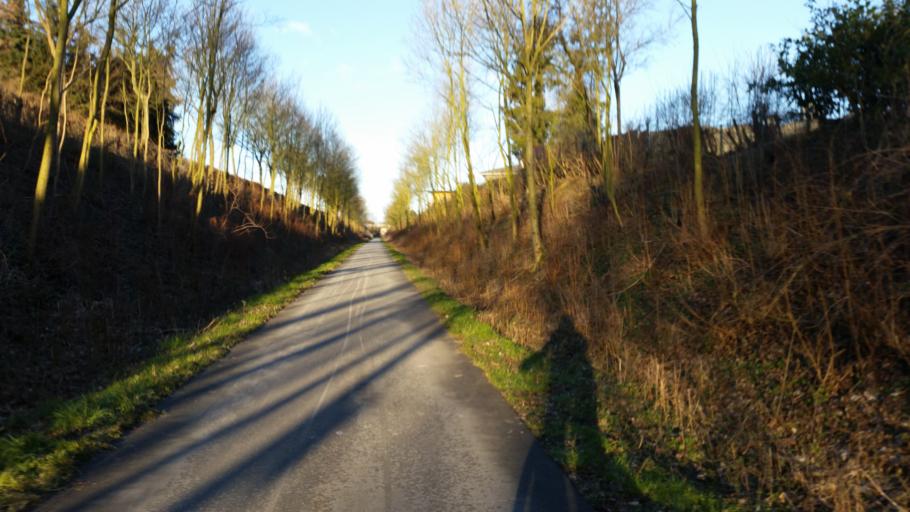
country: DE
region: North Rhine-Westphalia
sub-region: Regierungsbezirk Munster
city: Neuenkirchen
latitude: 52.2496
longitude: 7.3735
